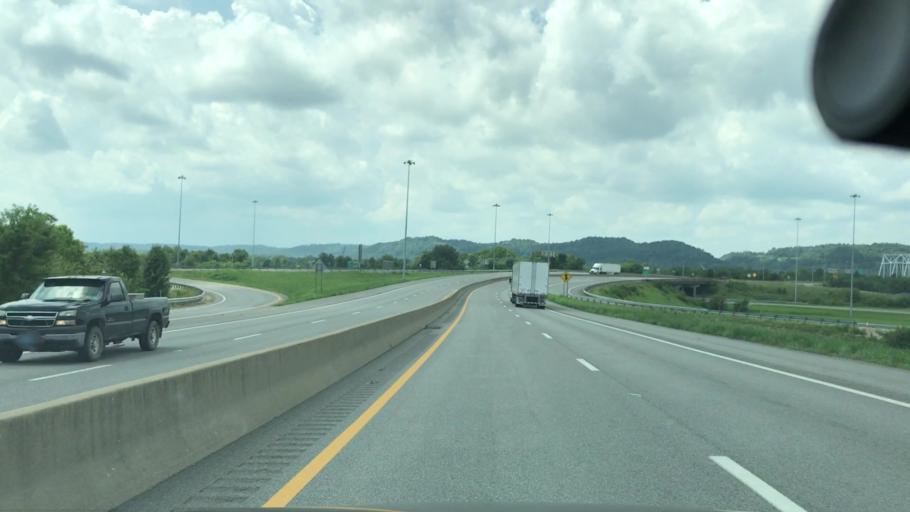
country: US
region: West Virginia
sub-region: Mason County
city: Point Pleasant
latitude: 38.8305
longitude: -82.1389
